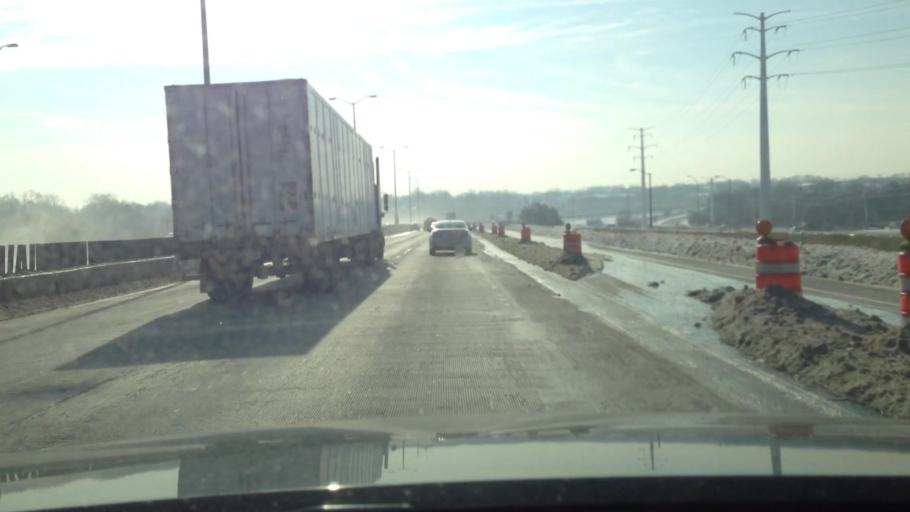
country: US
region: Illinois
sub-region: DuPage County
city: Downers Grove
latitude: 41.8201
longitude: -88.0283
